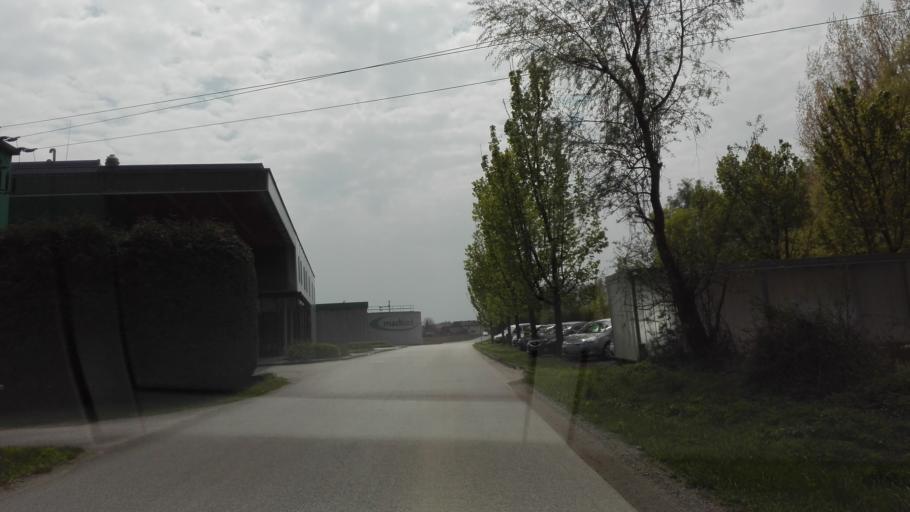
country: AT
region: Upper Austria
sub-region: Politischer Bezirk Perg
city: Perg
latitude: 48.2364
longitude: 14.5999
